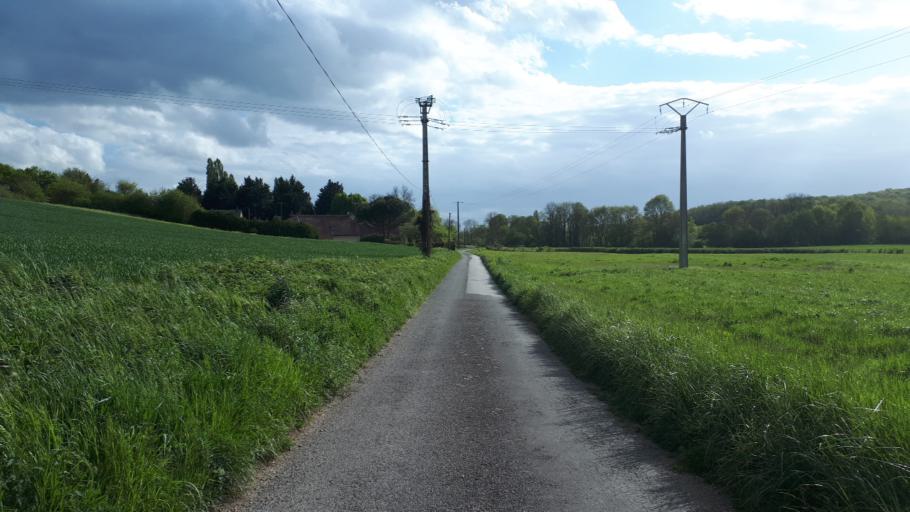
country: FR
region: Centre
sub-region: Departement du Loir-et-Cher
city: Aze
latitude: 47.8431
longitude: 0.9946
